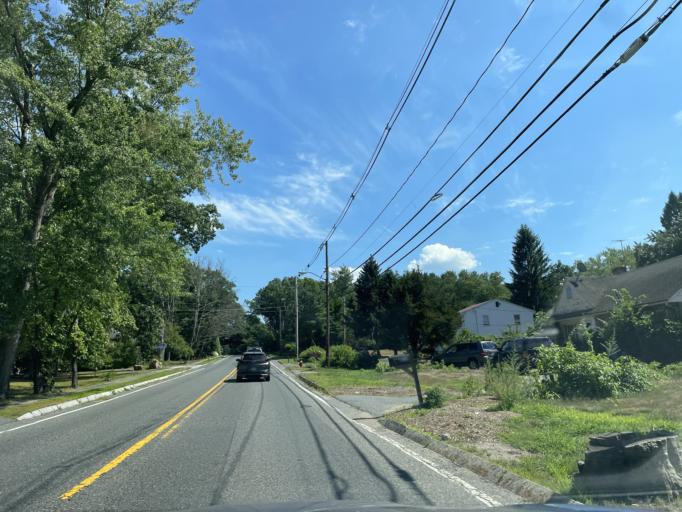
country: US
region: Massachusetts
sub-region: Middlesex County
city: Holliston
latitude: 42.2223
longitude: -71.4286
